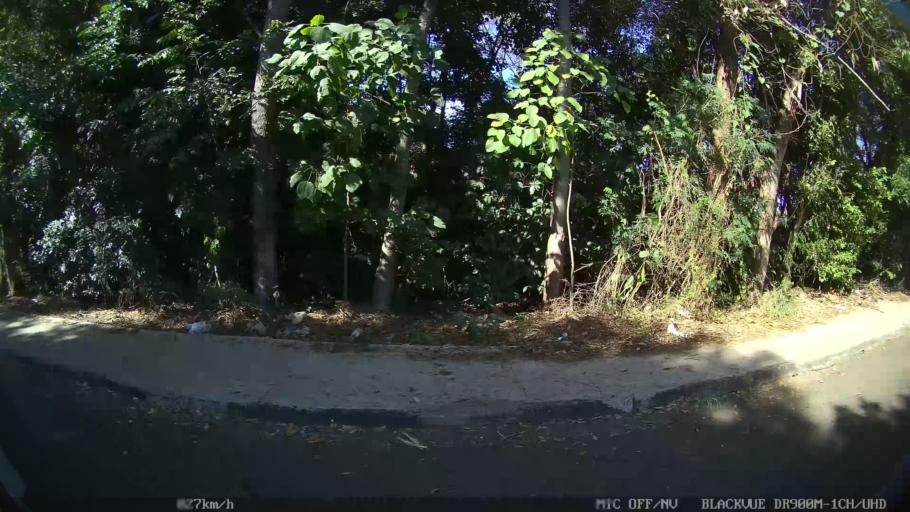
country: BR
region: Sao Paulo
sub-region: Franca
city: Franca
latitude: -20.4930
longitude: -47.4138
